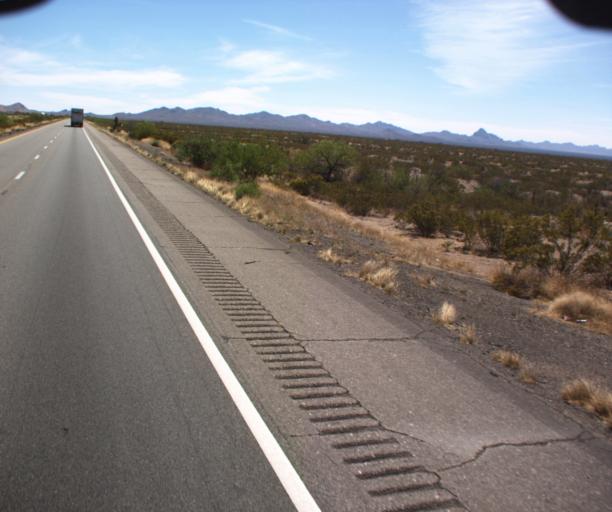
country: US
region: New Mexico
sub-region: Hidalgo County
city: Lordsburg
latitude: 32.2439
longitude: -109.1208
